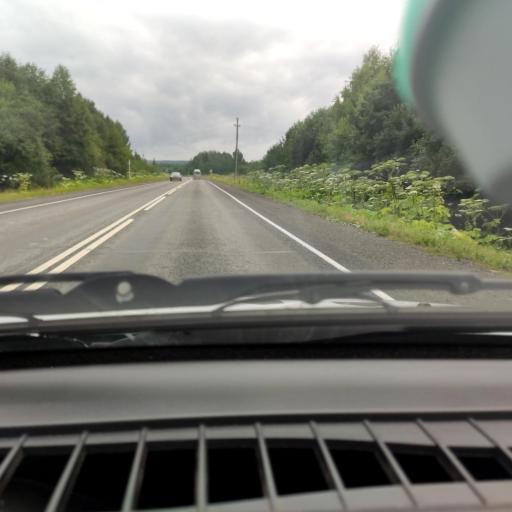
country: RU
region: Perm
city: Dobryanka
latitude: 58.8428
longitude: 56.7763
